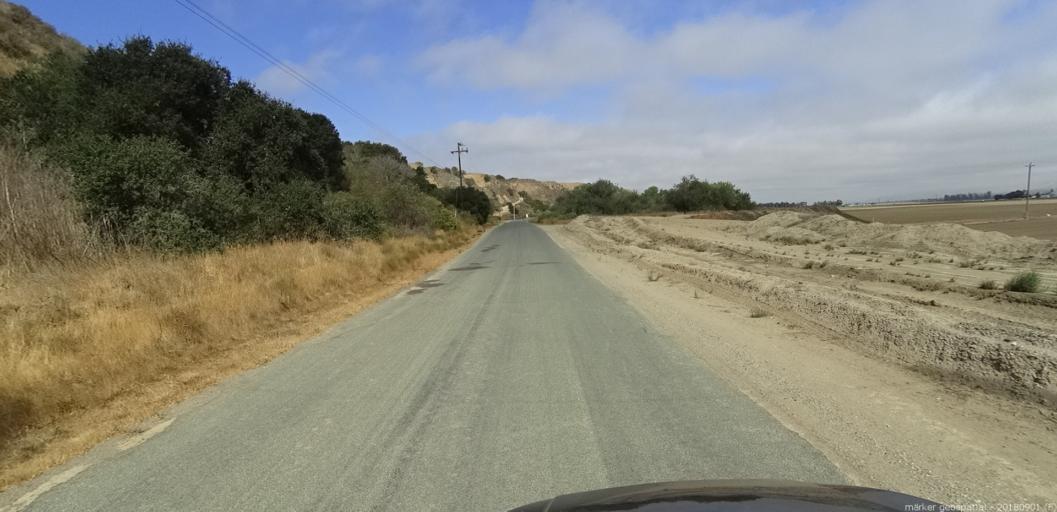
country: US
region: California
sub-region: Monterey County
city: Soledad
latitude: 36.3983
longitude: -121.3739
